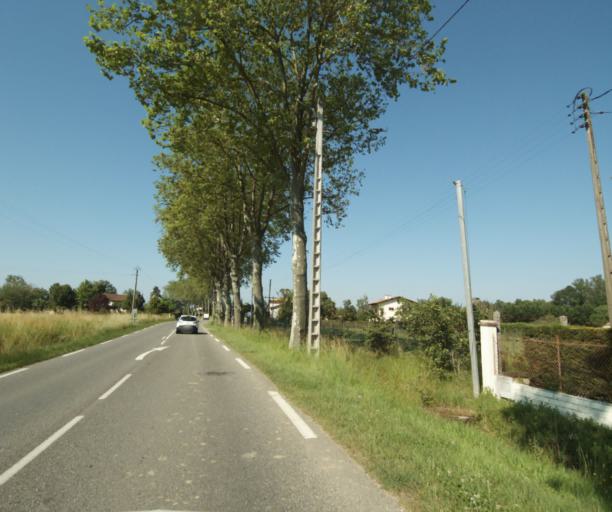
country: FR
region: Midi-Pyrenees
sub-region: Departement du Tarn-et-Garonne
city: Montauban
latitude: 44.0027
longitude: 1.3307
